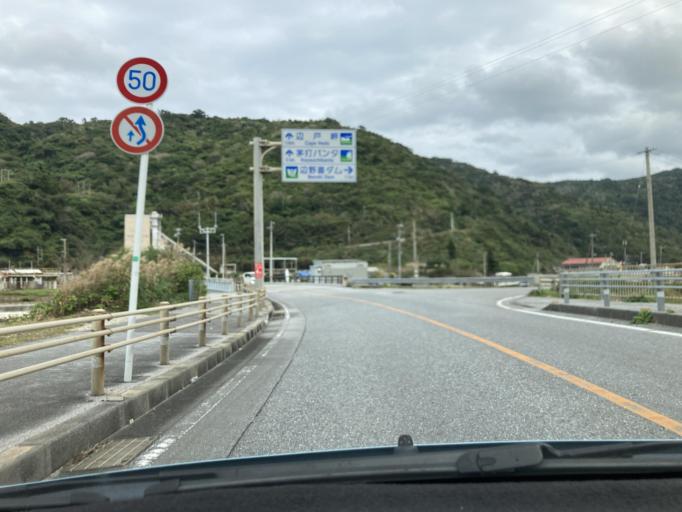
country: JP
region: Okinawa
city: Nago
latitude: 26.7972
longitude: 128.2316
